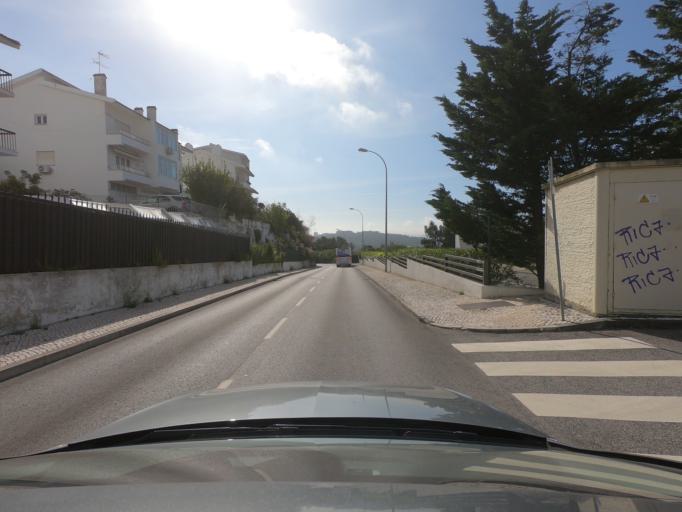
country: PT
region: Lisbon
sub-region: Oeiras
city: Quejas
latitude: 38.7153
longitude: -9.2623
